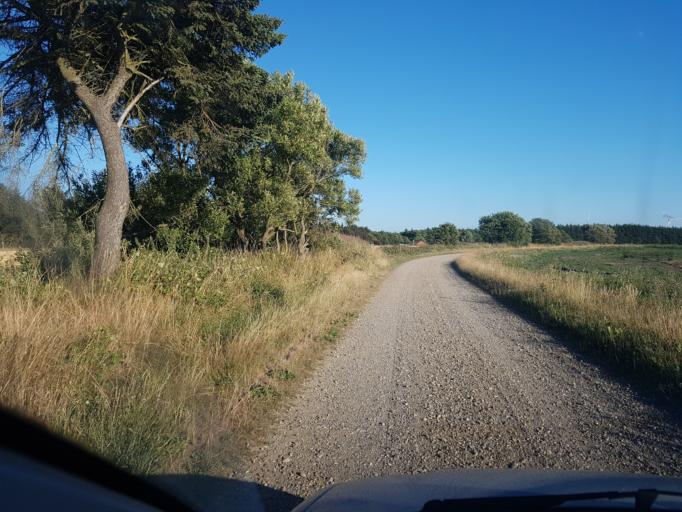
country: DK
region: South Denmark
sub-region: Esbjerg Kommune
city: Esbjerg
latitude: 55.4896
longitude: 8.5070
